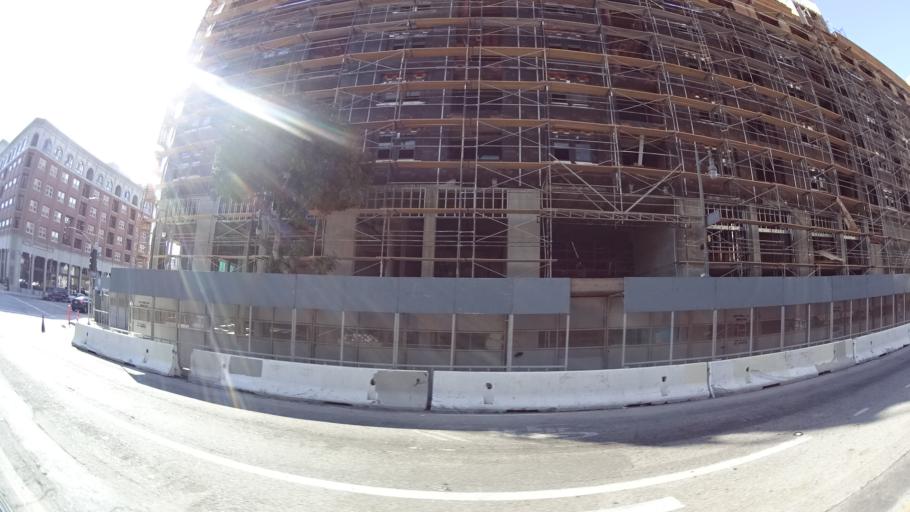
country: US
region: California
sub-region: Los Angeles County
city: Los Angeles
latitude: 34.0406
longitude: -118.2566
